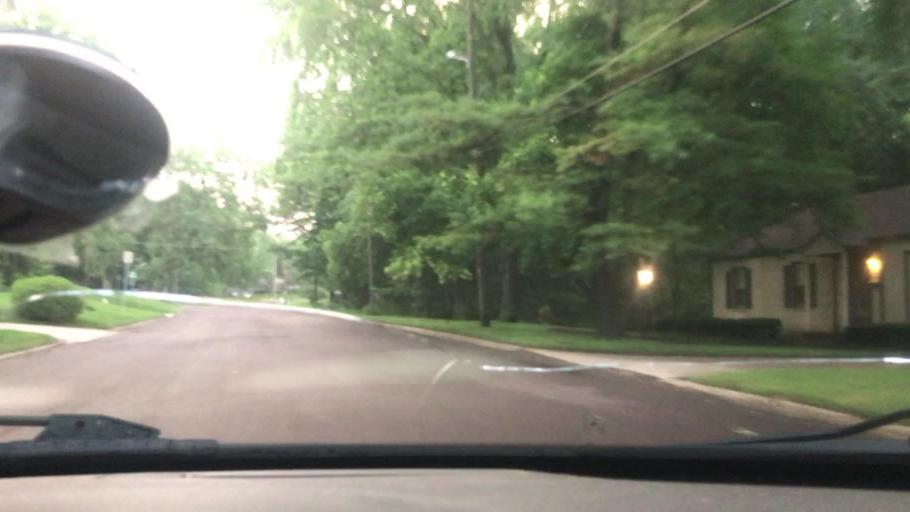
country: US
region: Illinois
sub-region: Tazewell County
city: Pekin
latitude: 40.5536
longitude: -89.6146
